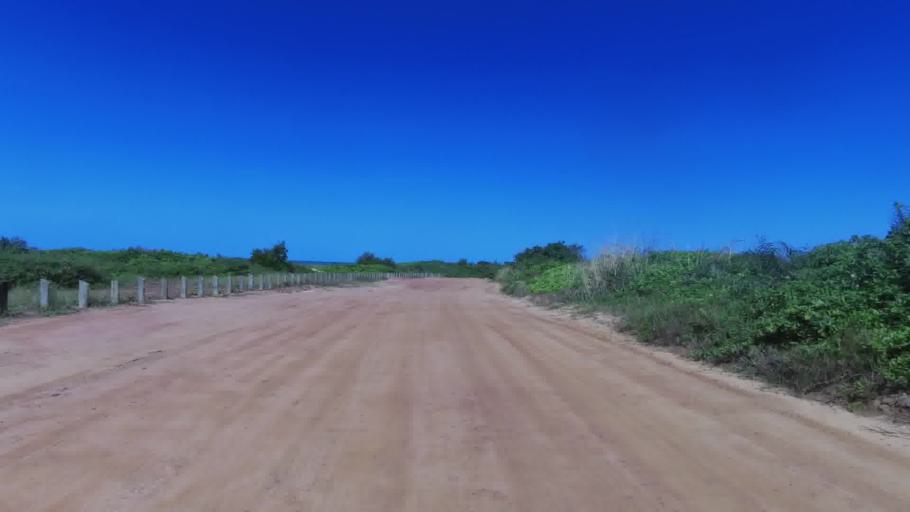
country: BR
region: Espirito Santo
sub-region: Piuma
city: Piuma
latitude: -20.8398
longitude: -40.6279
